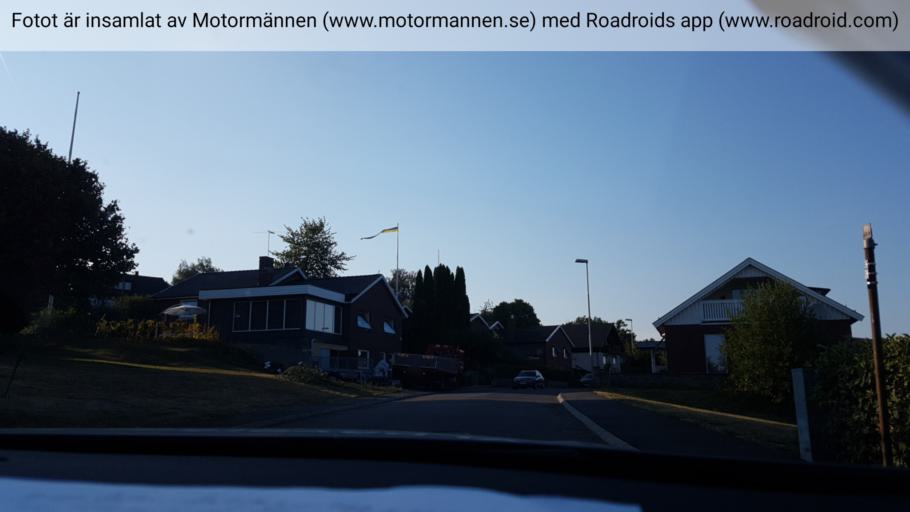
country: SE
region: Vaestra Goetaland
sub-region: Skovde Kommun
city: Skoevde
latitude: 58.3925
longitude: 13.8256
